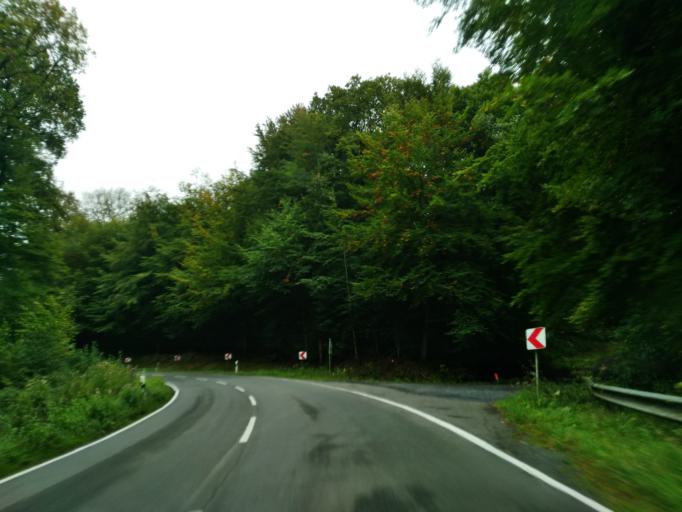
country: DE
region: North Rhine-Westphalia
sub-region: Regierungsbezirk Koln
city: Bad Honnef
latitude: 50.6736
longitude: 7.2770
